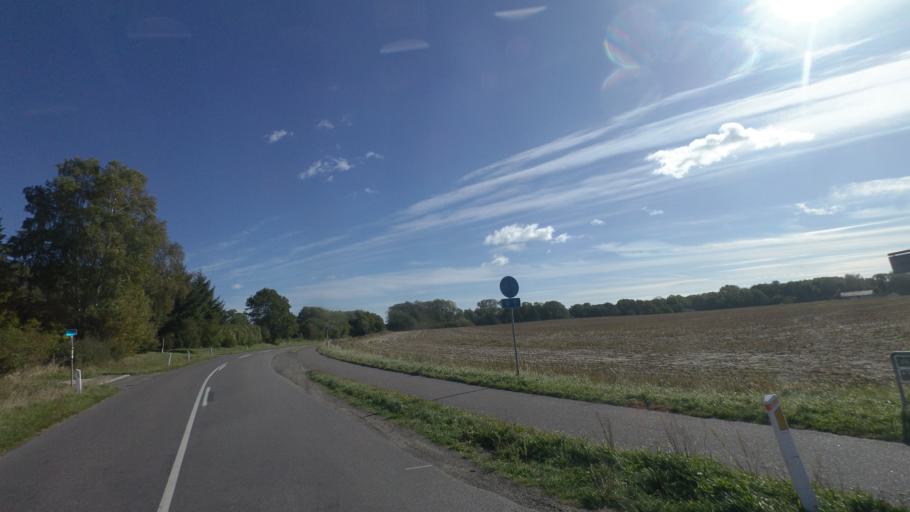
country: DK
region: Capital Region
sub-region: Bornholm Kommune
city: Akirkeby
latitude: 55.0092
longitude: 14.9922
